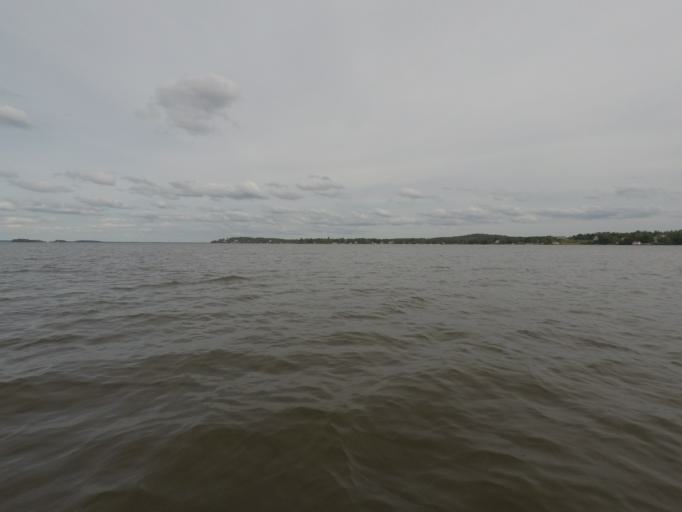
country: SE
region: Soedermanland
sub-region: Eskilstuna Kommun
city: Hallbybrunn
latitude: 59.4594
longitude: 16.4114
